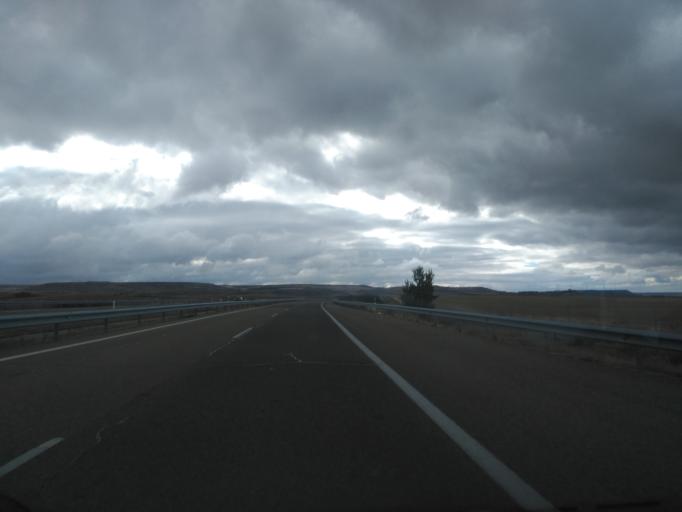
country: ES
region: Castille and Leon
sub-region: Provincia de Palencia
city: Amusco
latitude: 42.1446
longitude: -4.4690
